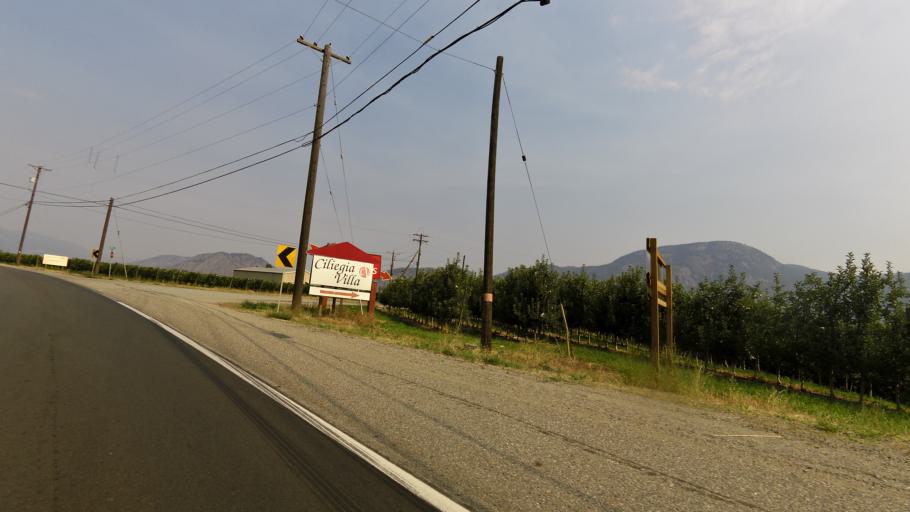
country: CA
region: British Columbia
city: Osoyoos
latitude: 49.0497
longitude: -119.4982
